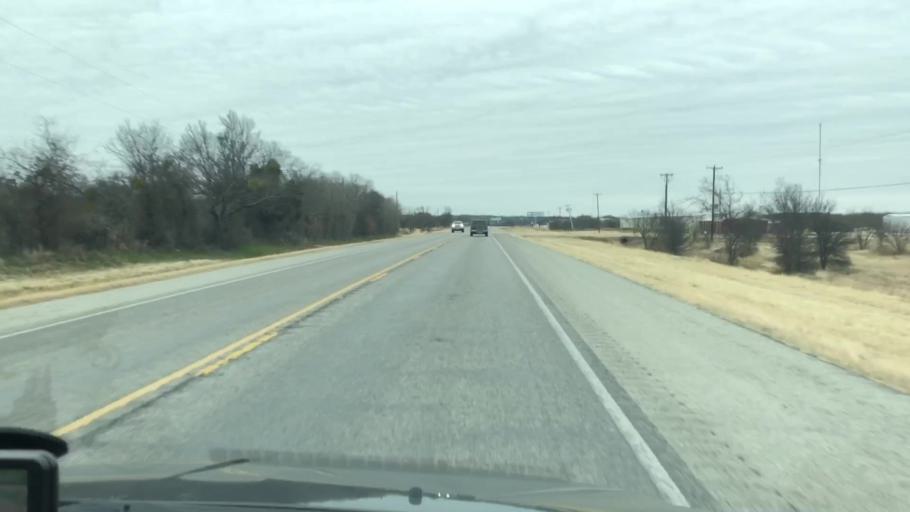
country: US
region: Texas
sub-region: Palo Pinto County
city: Mineral Wells
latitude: 32.8480
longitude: -98.0992
